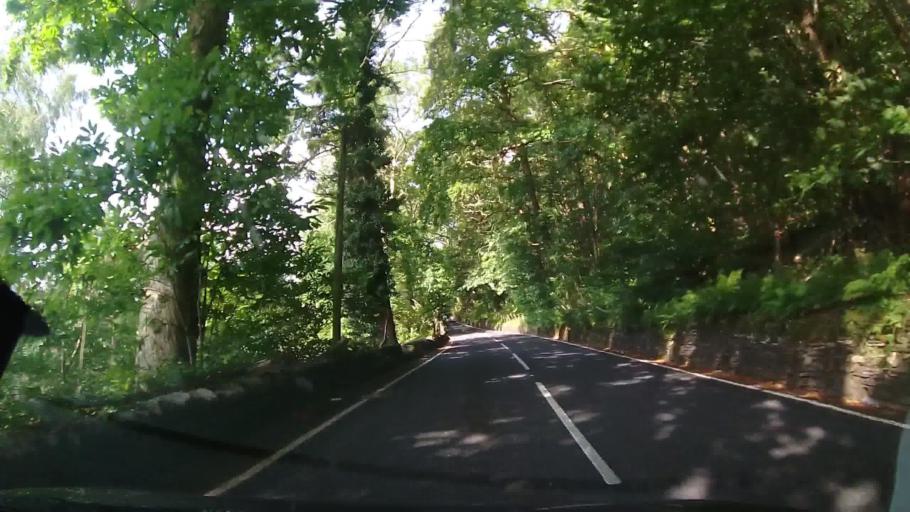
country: GB
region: Wales
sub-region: Gwynedd
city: Ffestiniog
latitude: 52.9569
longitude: -3.9545
